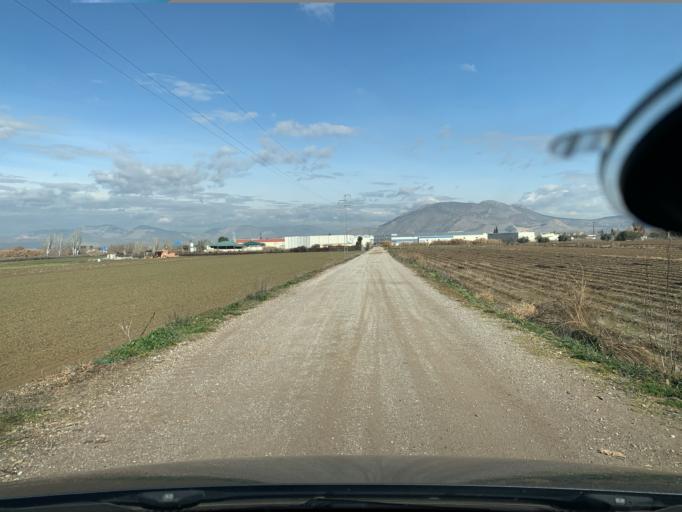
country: ES
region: Andalusia
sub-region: Provincia de Granada
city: Chauchina
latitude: 37.1848
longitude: -3.7496
